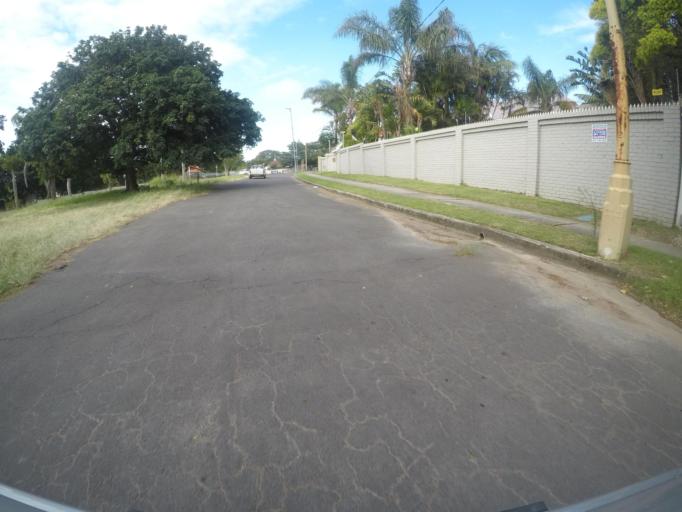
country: ZA
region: Eastern Cape
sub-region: Buffalo City Metropolitan Municipality
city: East London
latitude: -32.9940
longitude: 27.9030
